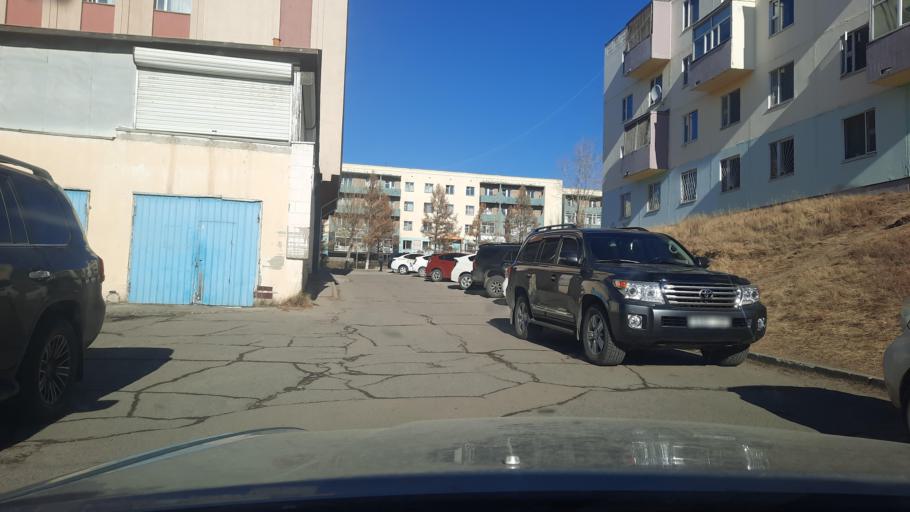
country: MN
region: Orhon
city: Erdenet
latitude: 49.0304
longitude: 104.0574
